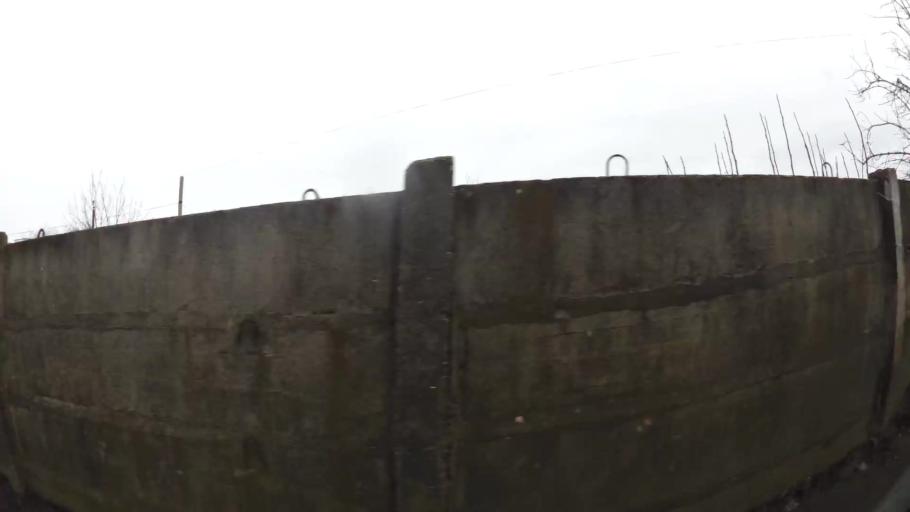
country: RO
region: Ilfov
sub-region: Comuna Otopeni
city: Otopeni
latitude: 44.5491
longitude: 26.0924
